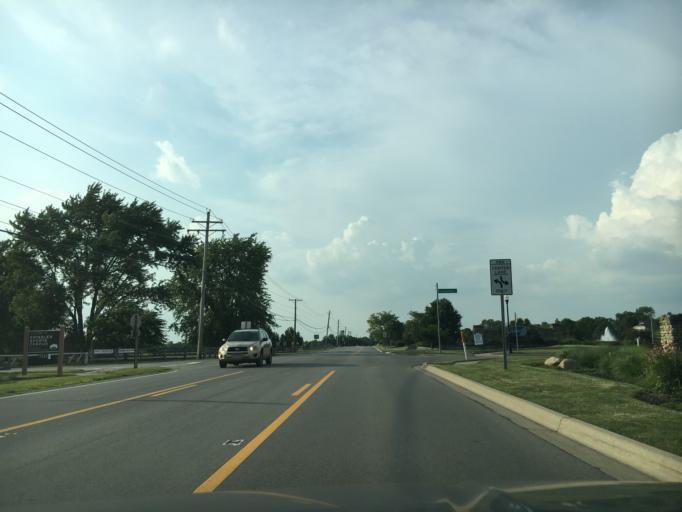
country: US
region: Ohio
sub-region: Franklin County
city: Hilliard
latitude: 39.9920
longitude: -83.1654
